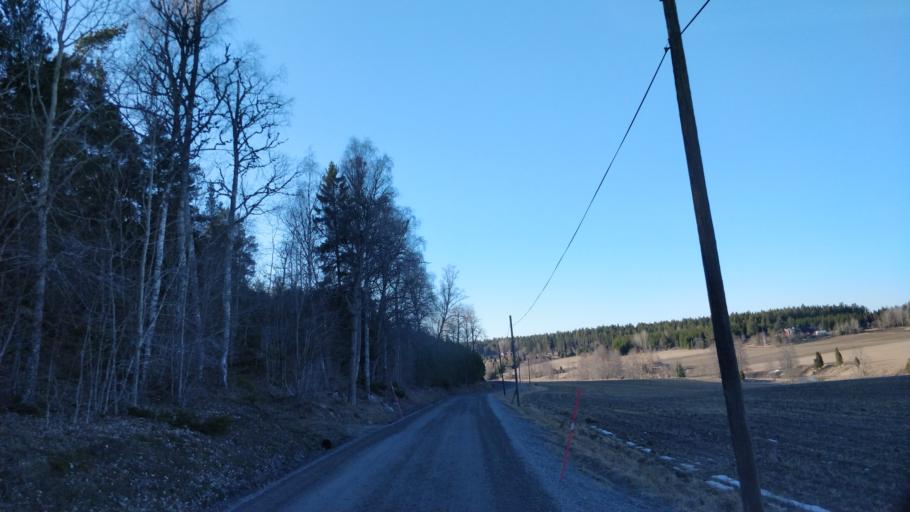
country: SE
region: Uppsala
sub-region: Enkopings Kommun
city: Orsundsbro
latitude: 59.7570
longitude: 17.1701
